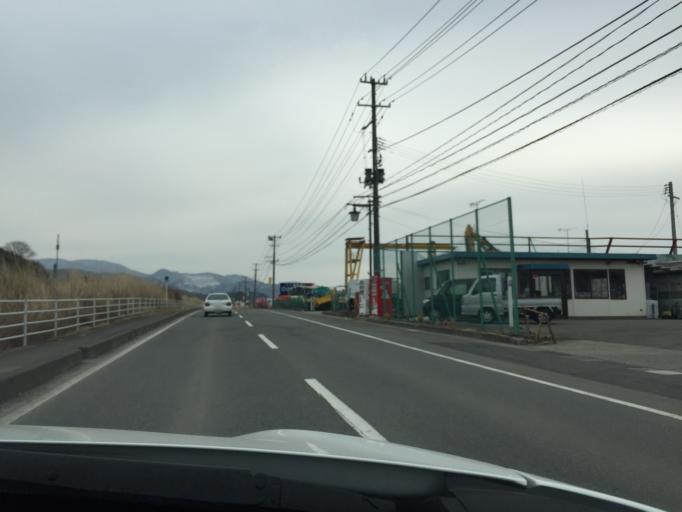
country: JP
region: Fukushima
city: Funehikimachi-funehiki
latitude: 37.4086
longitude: 140.6122
